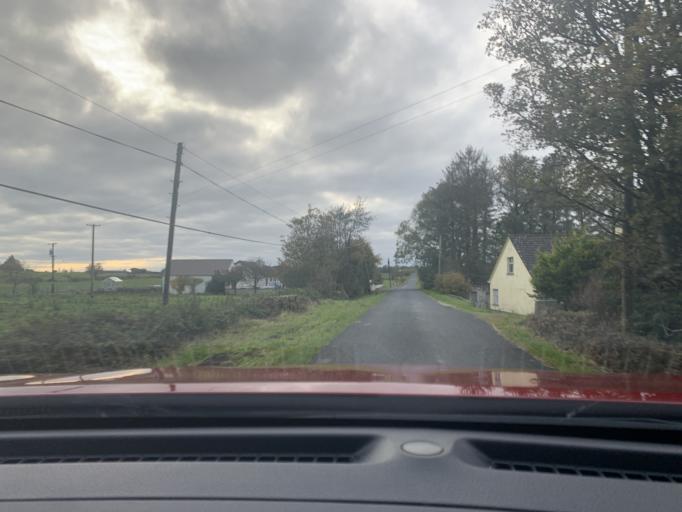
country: IE
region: Connaught
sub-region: Sligo
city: Tobercurry
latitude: 54.0289
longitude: -8.6808
